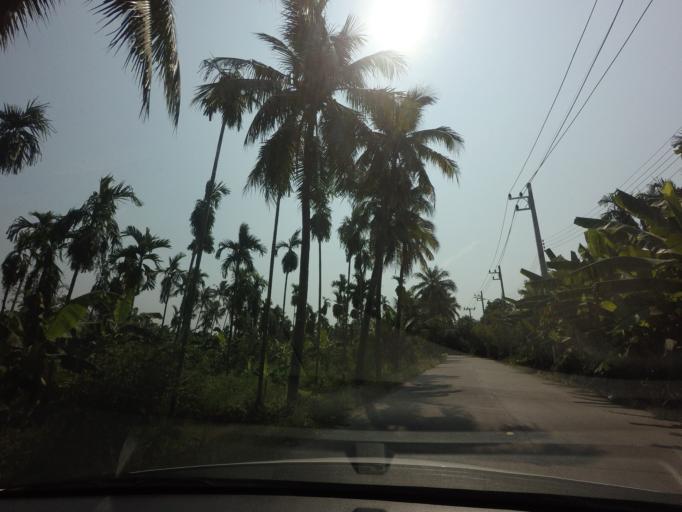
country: TH
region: Nakhon Pathom
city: Sam Phran
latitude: 13.7550
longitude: 100.2622
